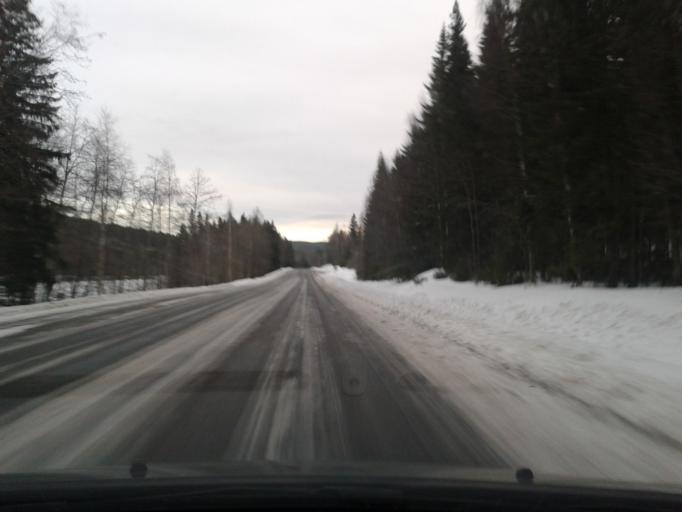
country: SE
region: Vaesternorrland
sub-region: Solleftea Kommun
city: Solleftea
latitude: 63.3040
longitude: 17.2058
